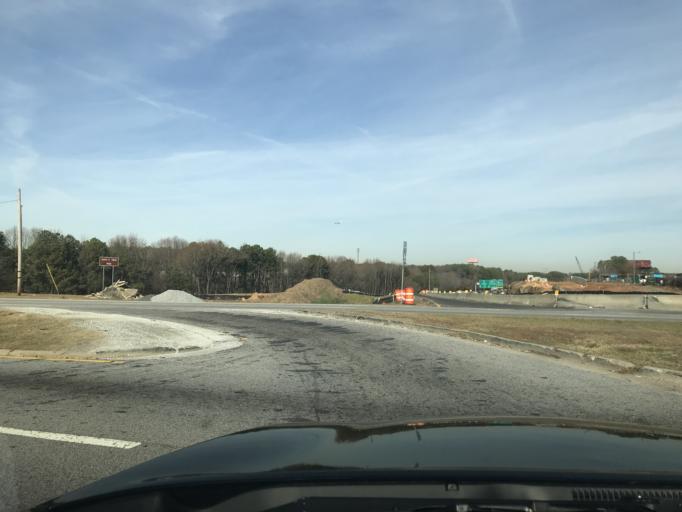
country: US
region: Georgia
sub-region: Clayton County
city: Forest Park
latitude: 33.6177
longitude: -84.3973
